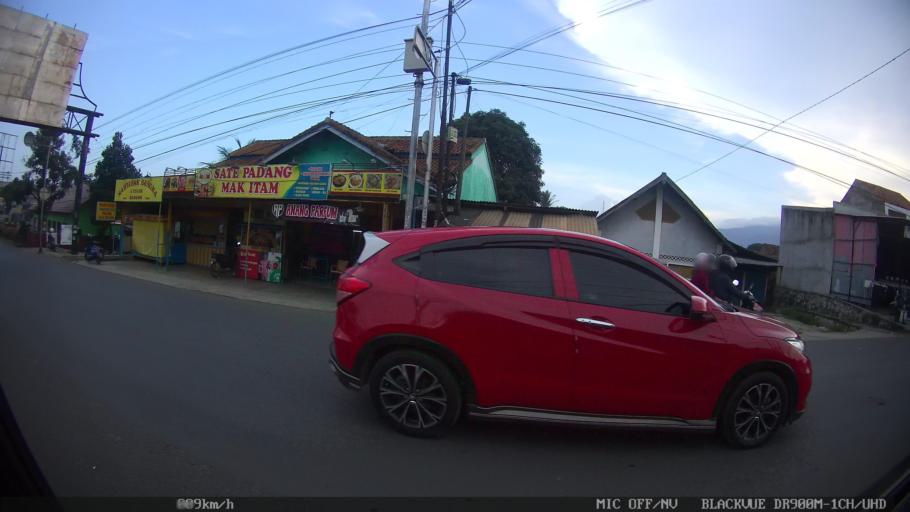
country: ID
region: Lampung
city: Kedaton
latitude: -5.3921
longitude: 105.2146
